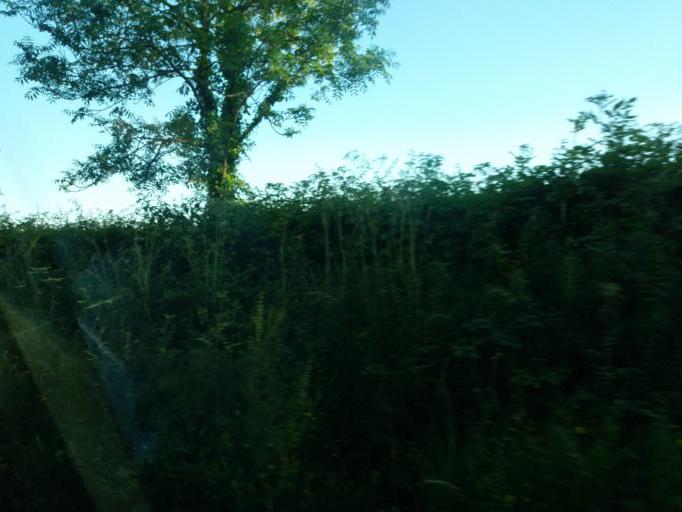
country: IE
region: Leinster
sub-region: An Mhi
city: Ashbourne
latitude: 53.5742
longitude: -6.3546
